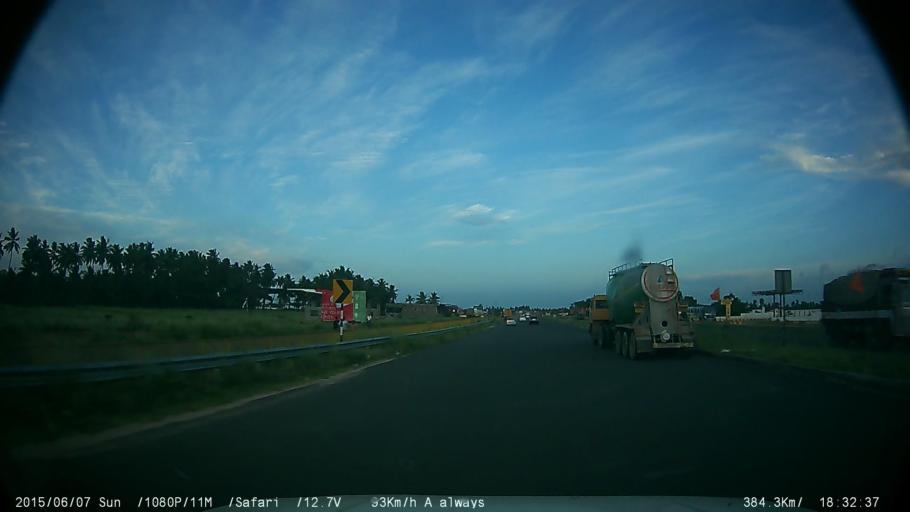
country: IN
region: Tamil Nadu
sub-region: Tiruppur
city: Avinashi
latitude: 11.1758
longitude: 77.2611
